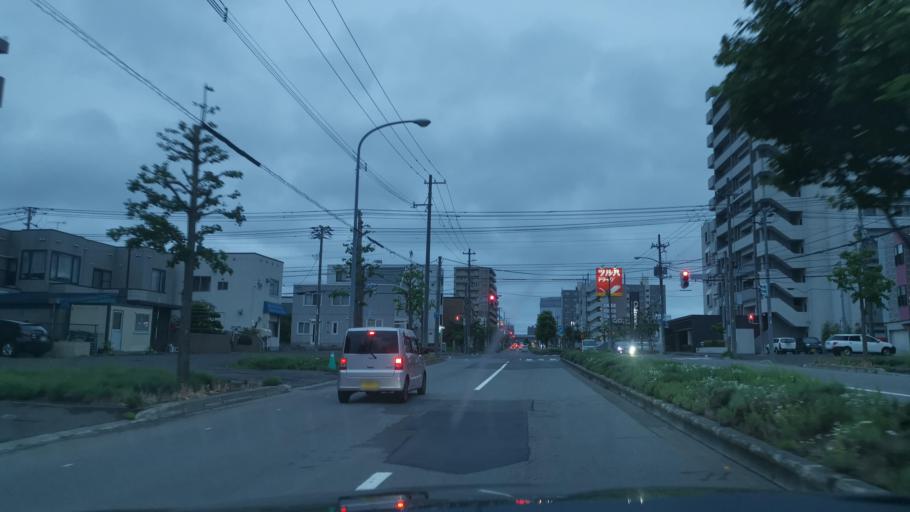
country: JP
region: Hokkaido
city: Sapporo
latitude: 43.0955
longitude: 141.2678
